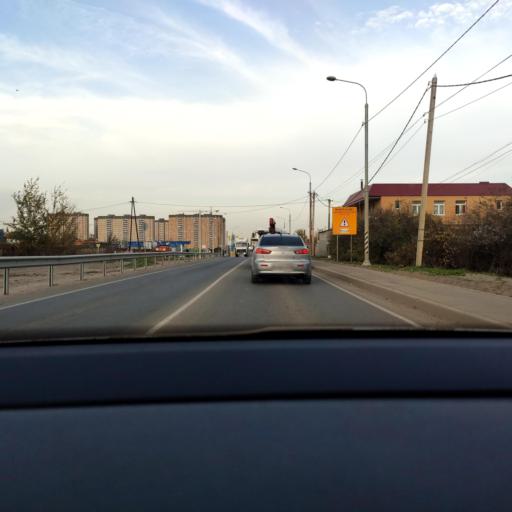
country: RU
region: Moskovskaya
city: Pirogovskiy
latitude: 55.9702
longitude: 37.7511
